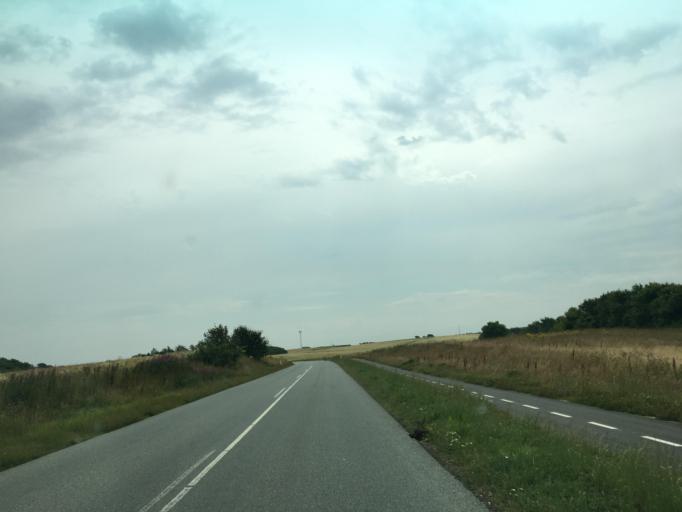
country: DK
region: North Denmark
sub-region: Thisted Kommune
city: Hurup
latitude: 56.7871
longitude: 8.4146
